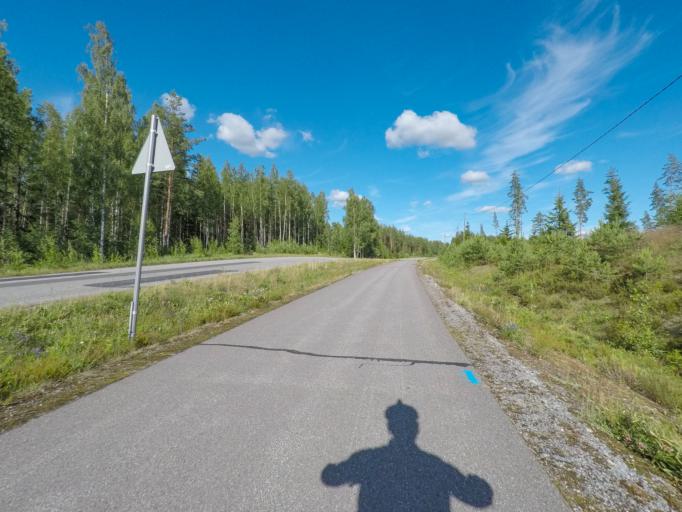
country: FI
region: South Karelia
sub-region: Lappeenranta
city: Joutseno
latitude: 61.1534
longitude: 28.5737
